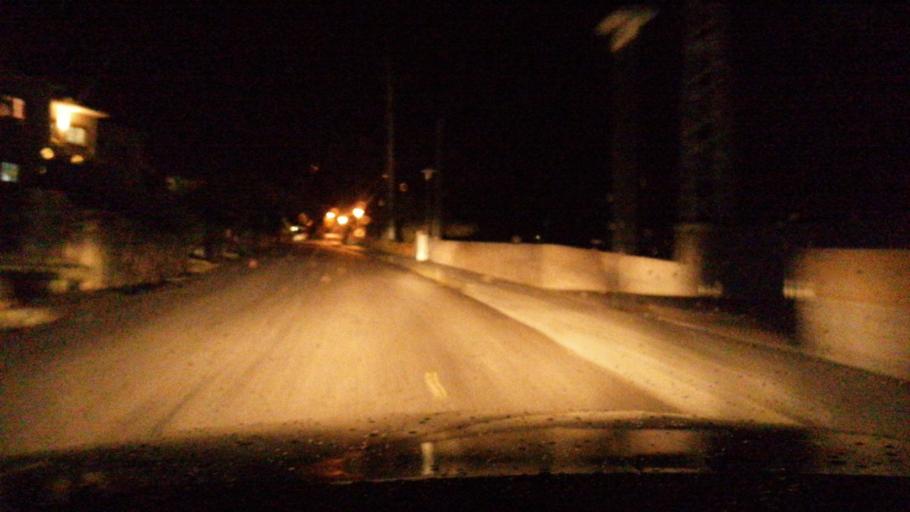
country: PT
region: Viseu
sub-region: Armamar
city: Armamar
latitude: 41.0651
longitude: -7.6445
